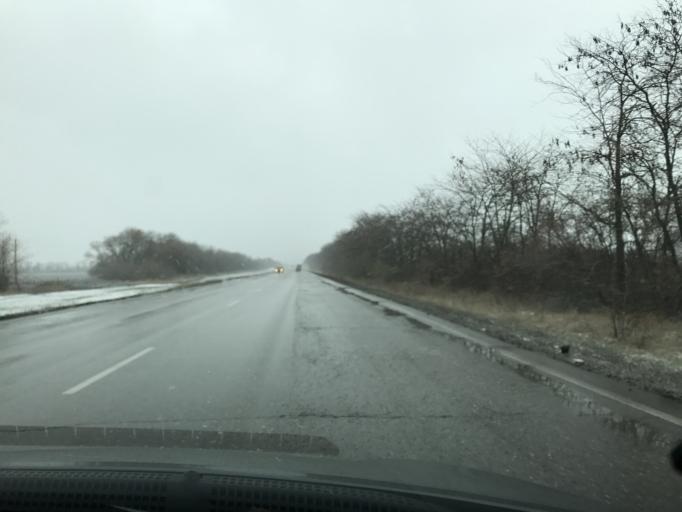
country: RU
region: Rostov
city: Kirovskaya
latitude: 47.0034
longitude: 39.9693
